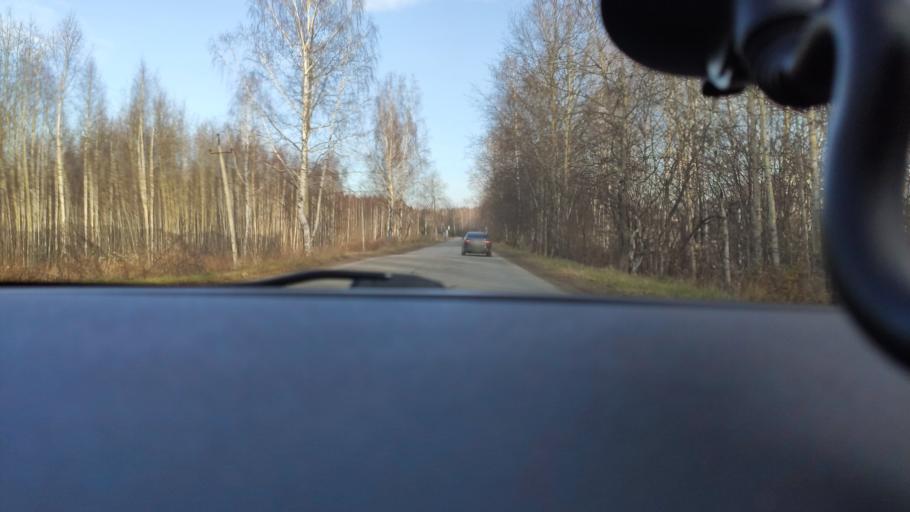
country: RU
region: Perm
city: Kondratovo
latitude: 58.0565
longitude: 56.0278
